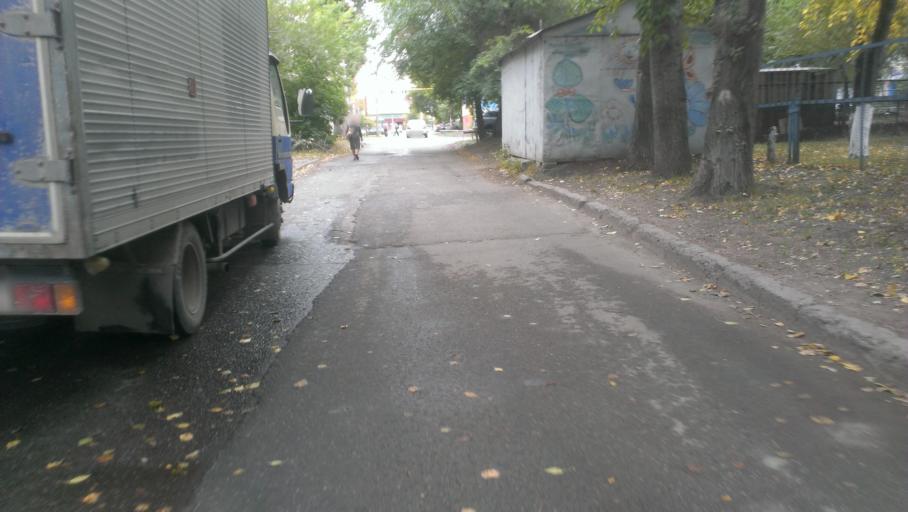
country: RU
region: Altai Krai
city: Novosilikatnyy
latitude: 53.3682
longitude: 83.6790
